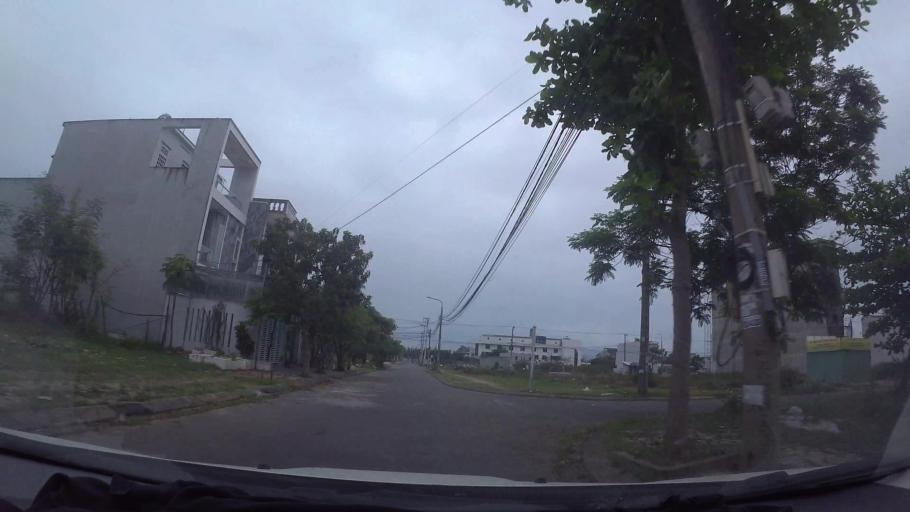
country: VN
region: Da Nang
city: Lien Chieu
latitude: 16.0869
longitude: 108.1502
